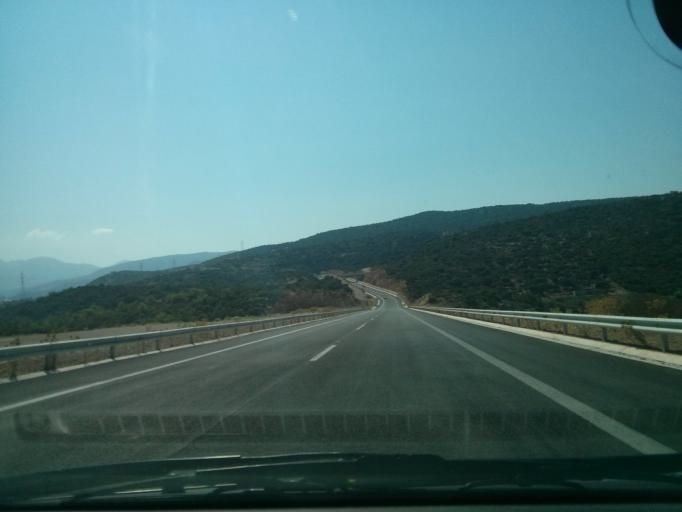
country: GR
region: Crete
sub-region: Nomos Lasithiou
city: Agios Nikolaos
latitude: 35.1699
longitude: 25.7021
